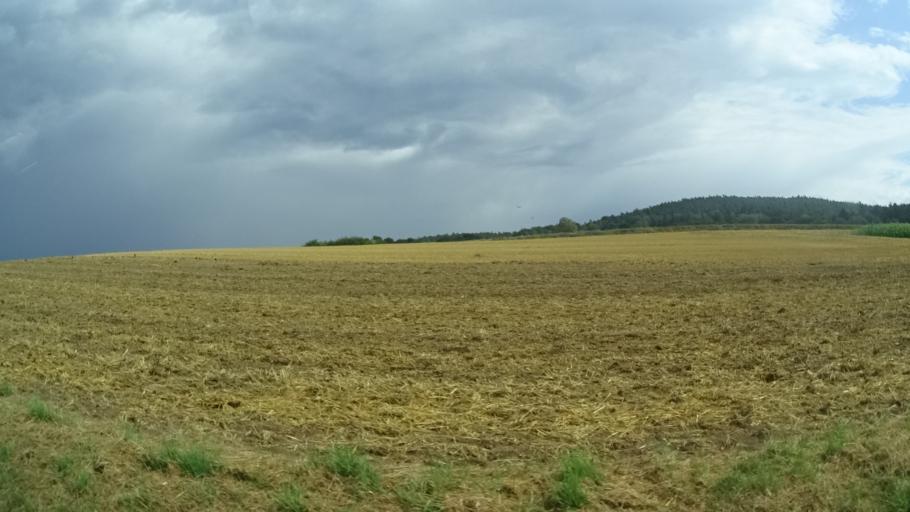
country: DE
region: Hesse
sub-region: Regierungsbezirk Kassel
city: Niederaula
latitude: 50.8044
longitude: 9.6383
